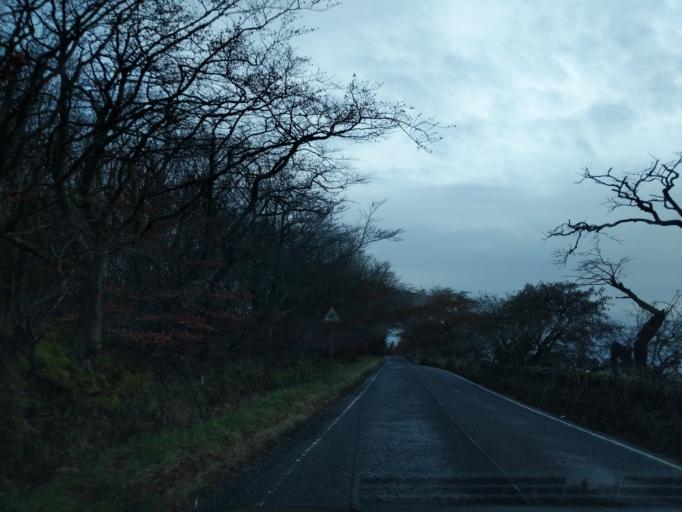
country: GB
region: Scotland
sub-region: West Lothian
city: Linlithgow
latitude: 55.9389
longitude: -3.6219
